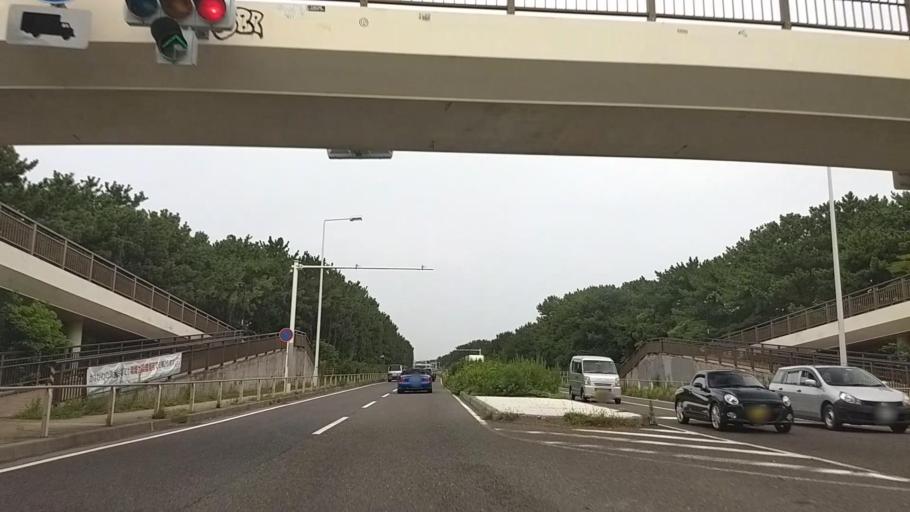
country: JP
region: Kanagawa
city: Chigasaki
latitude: 35.3180
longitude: 139.4153
